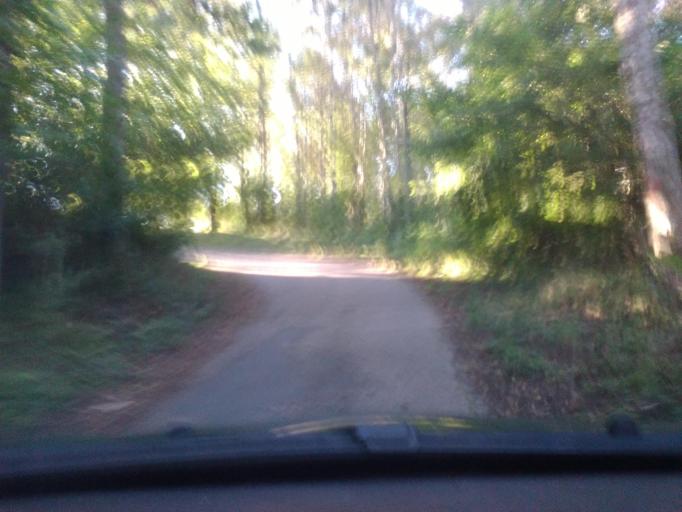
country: FR
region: Lorraine
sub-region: Departement des Vosges
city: Senones
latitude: 48.3756
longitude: 7.0311
